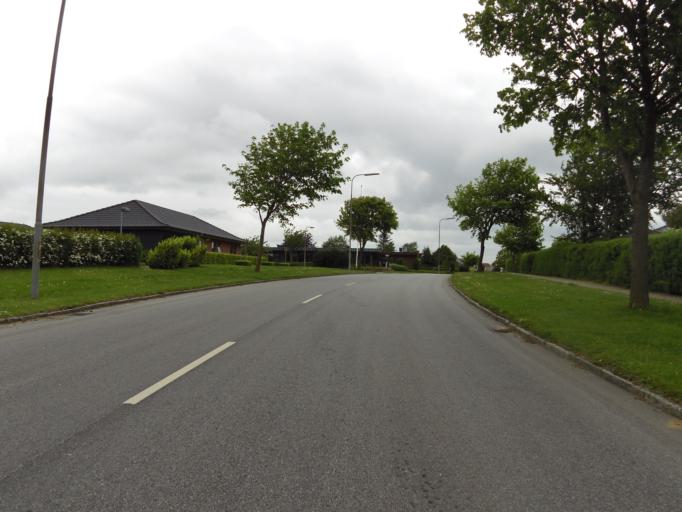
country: DK
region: South Denmark
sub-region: Tonder Kommune
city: Toftlund
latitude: 55.1899
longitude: 9.0595
